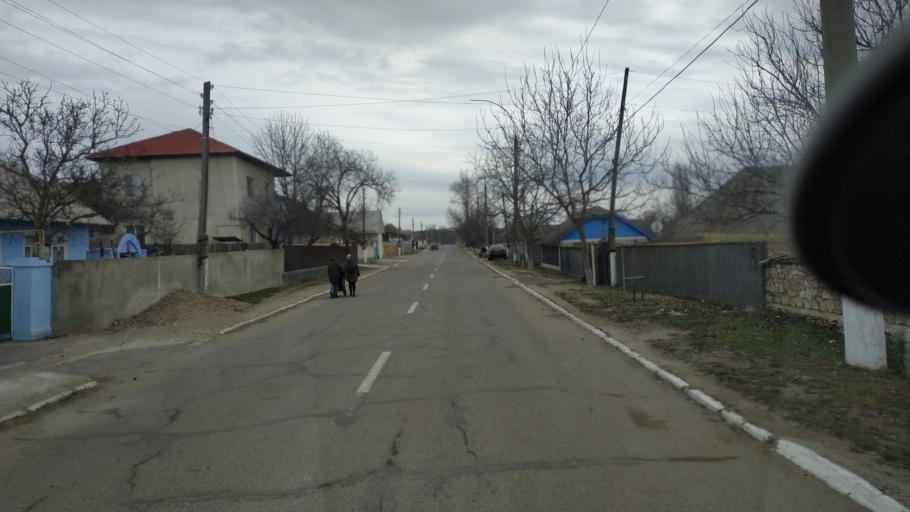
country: MD
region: Telenesti
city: Cocieri
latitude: 47.3425
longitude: 29.1165
